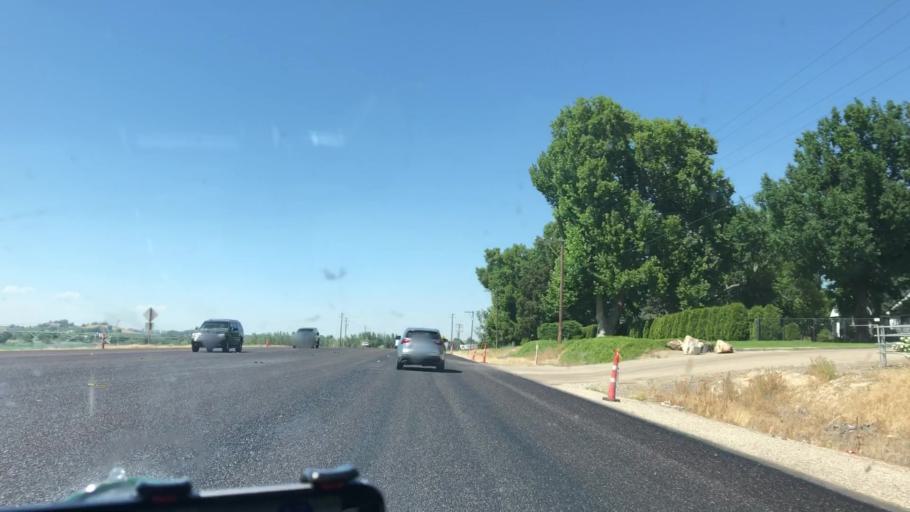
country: US
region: Idaho
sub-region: Owyhee County
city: Marsing
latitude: 43.5748
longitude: -116.7924
